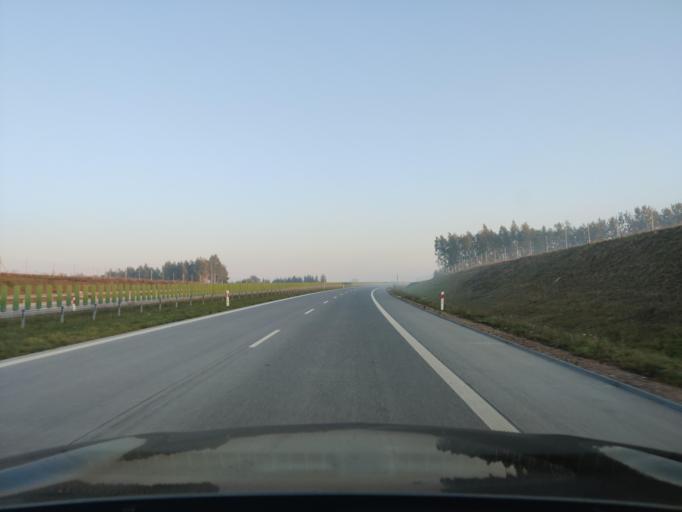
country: PL
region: Masovian Voivodeship
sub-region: Powiat mlawski
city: Wisniewo
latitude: 53.0072
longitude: 20.3389
